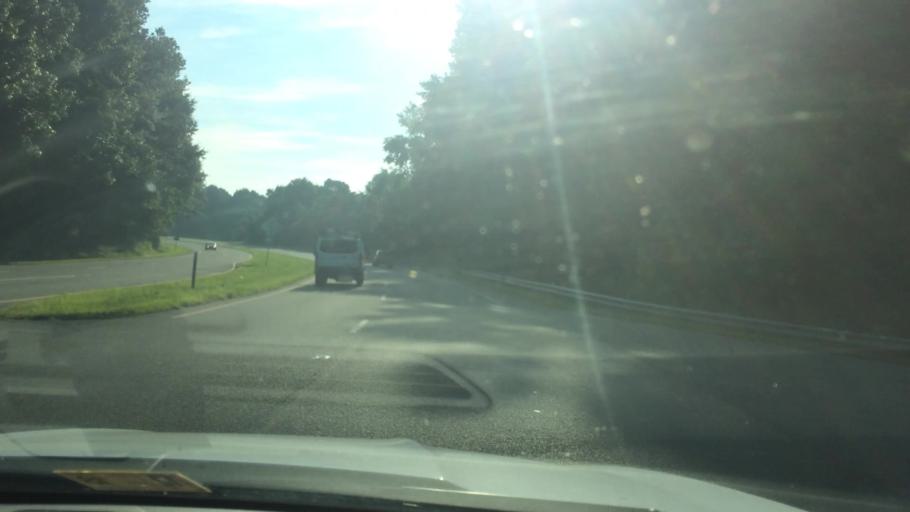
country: US
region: Virginia
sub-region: Gloucester County
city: Gloucester Courthouse
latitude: 37.4251
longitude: -76.4881
